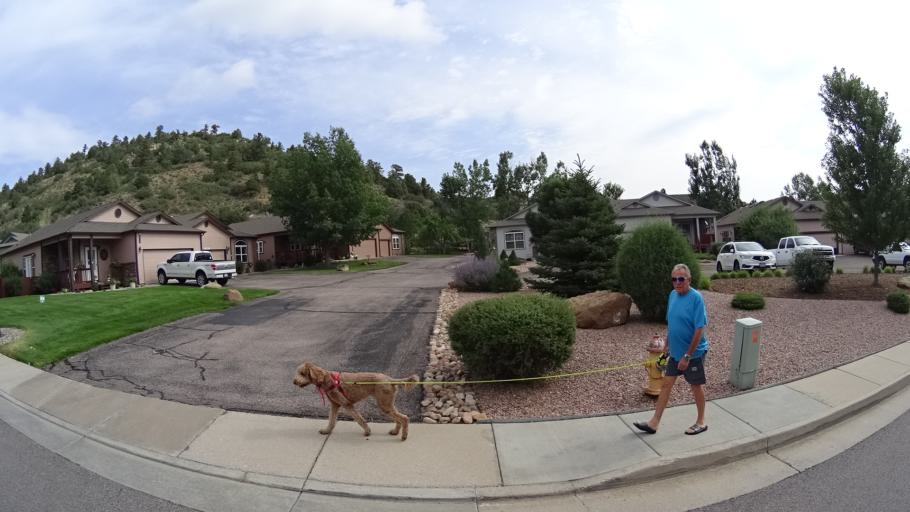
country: US
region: Colorado
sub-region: El Paso County
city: Colorado Springs
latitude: 38.8944
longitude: -104.7899
